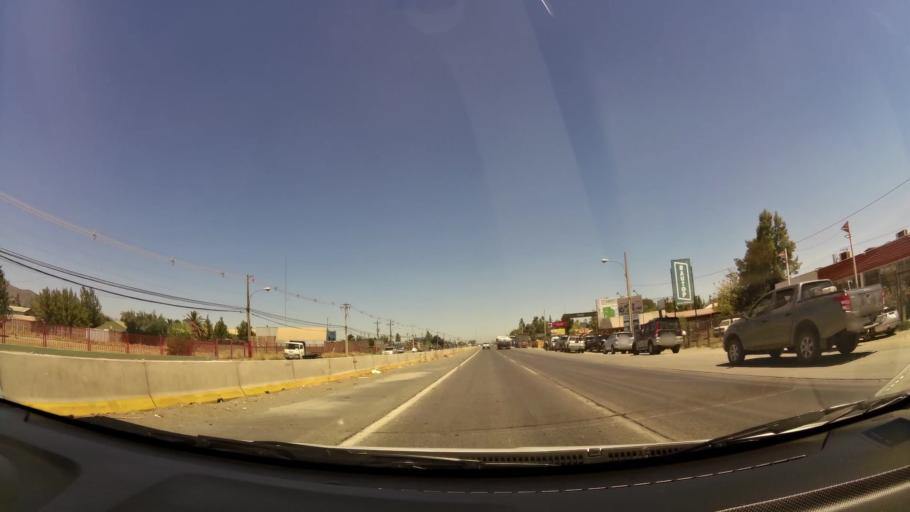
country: CL
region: O'Higgins
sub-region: Provincia de Cachapoal
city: Rancagua
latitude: -34.2045
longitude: -70.7633
